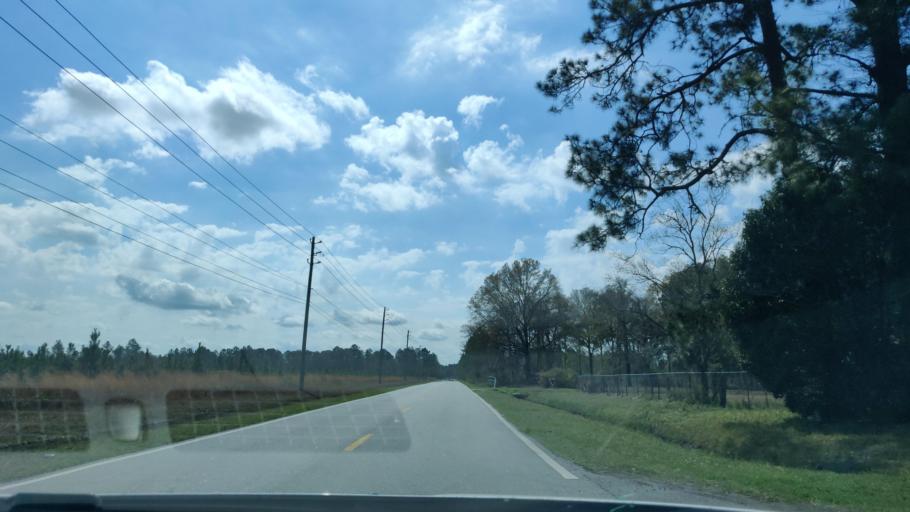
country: US
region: Florida
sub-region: Duval County
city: Baldwin
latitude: 30.2289
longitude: -81.9411
